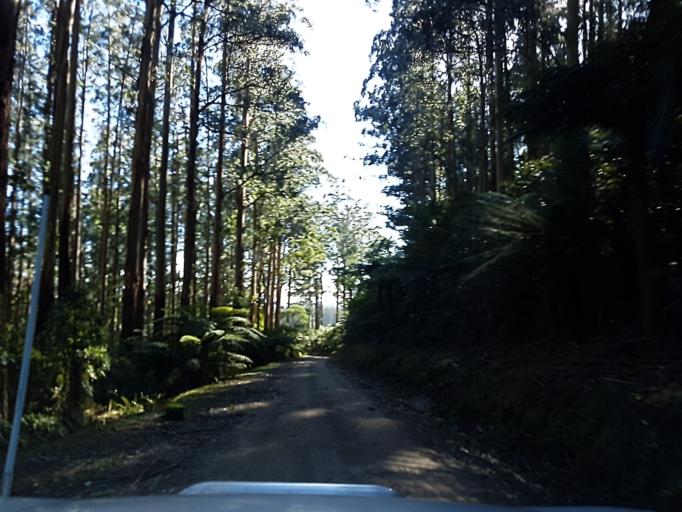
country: AU
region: Victoria
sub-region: Yarra Ranges
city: Healesville
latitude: -37.5721
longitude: 145.5201
